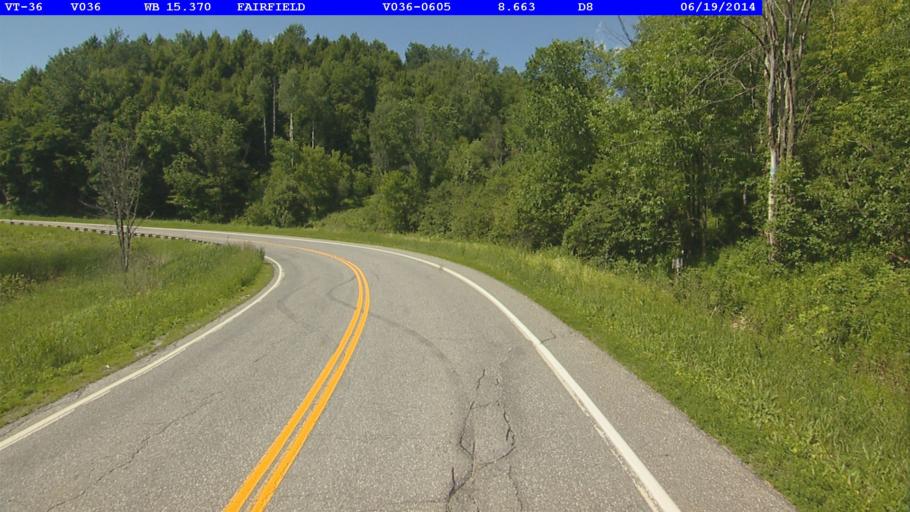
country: US
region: Vermont
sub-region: Franklin County
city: Enosburg Falls
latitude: 44.7924
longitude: -72.8703
